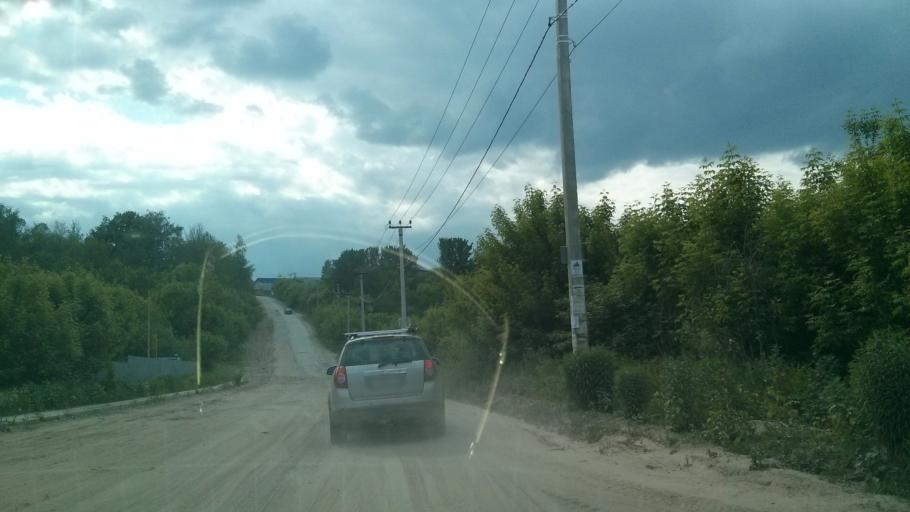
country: RU
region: Nizjnij Novgorod
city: Afonino
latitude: 56.2731
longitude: 44.0997
